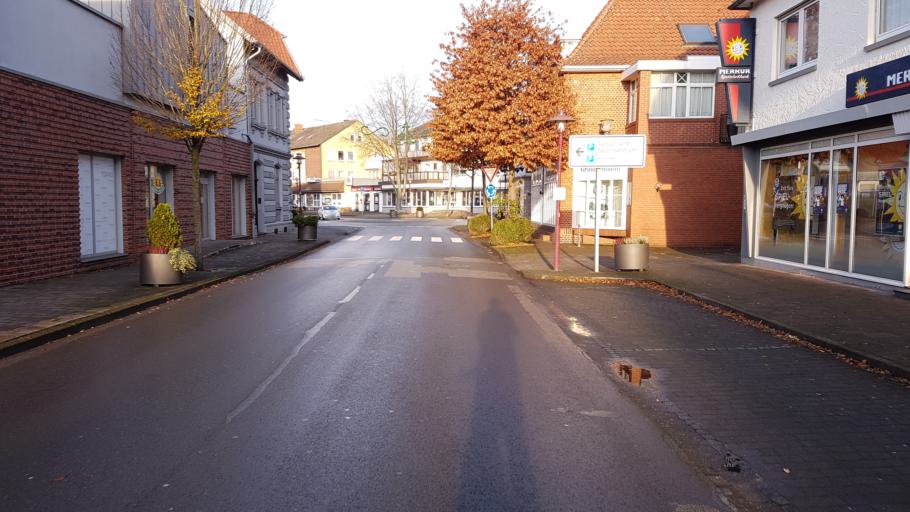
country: DE
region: North Rhine-Westphalia
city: Rahden
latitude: 52.4329
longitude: 8.6172
